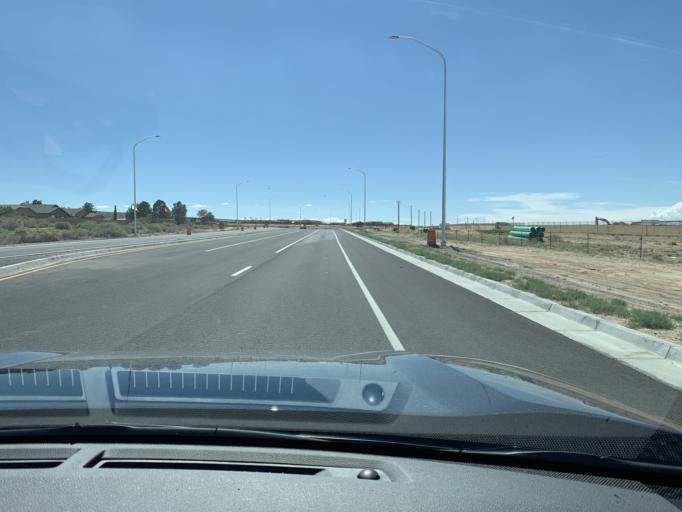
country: US
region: New Mexico
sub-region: Valencia County
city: Los Lunas
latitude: 34.8204
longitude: -106.7901
